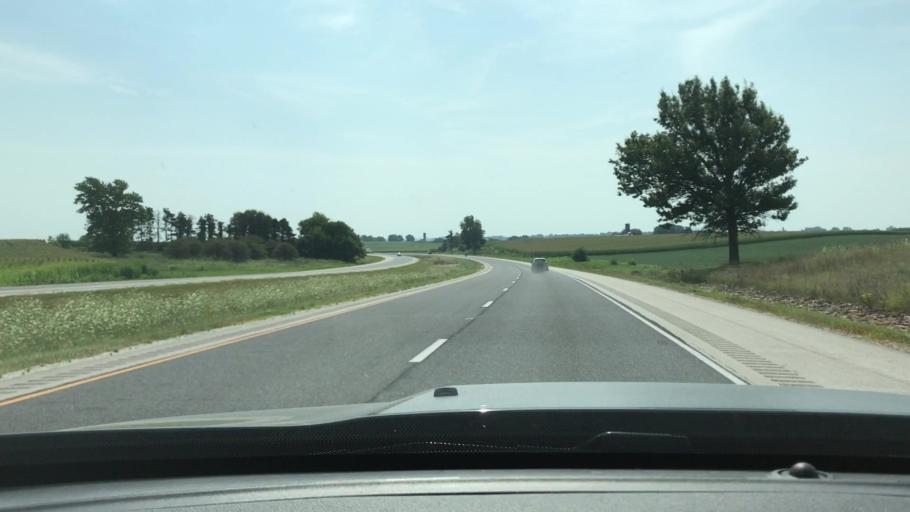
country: US
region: Illinois
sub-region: Henry County
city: Geneseo
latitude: 41.4187
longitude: -90.1376
